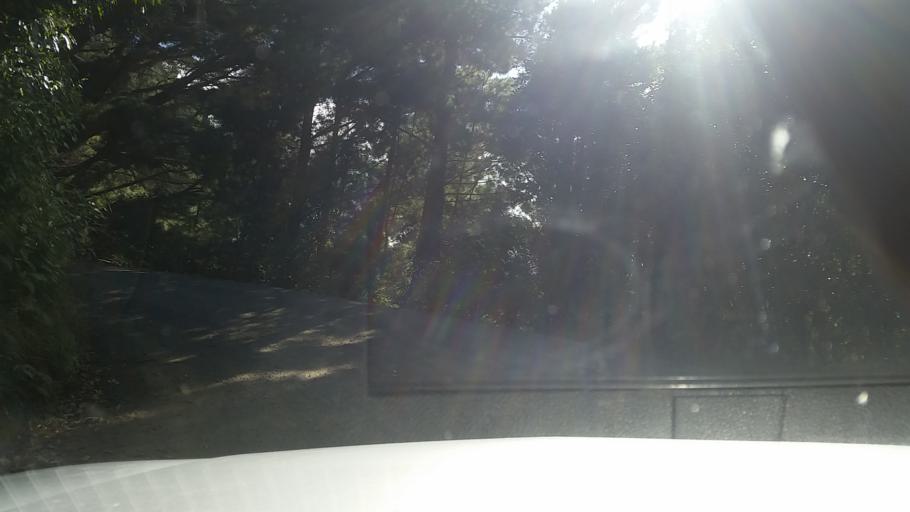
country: NZ
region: Marlborough
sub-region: Marlborough District
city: Picton
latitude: -41.2959
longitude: 174.1240
